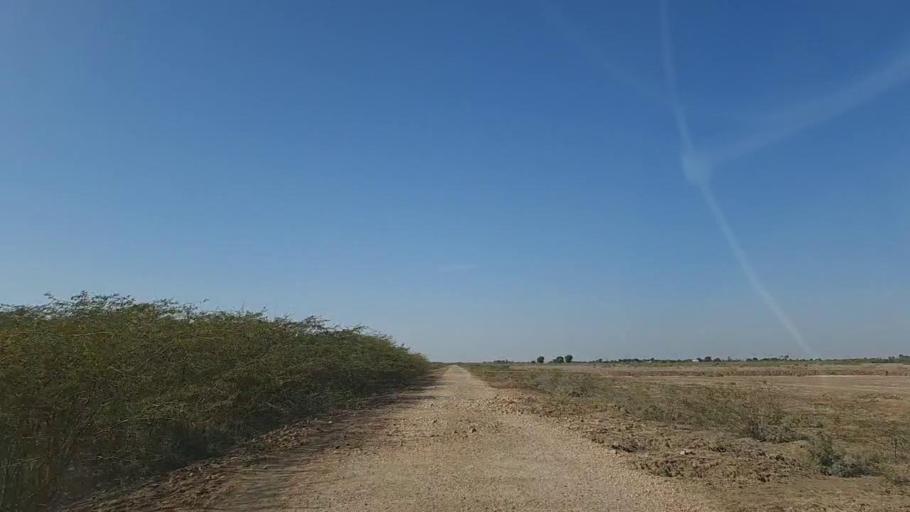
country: PK
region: Sindh
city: Kunri
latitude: 25.2403
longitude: 69.4992
